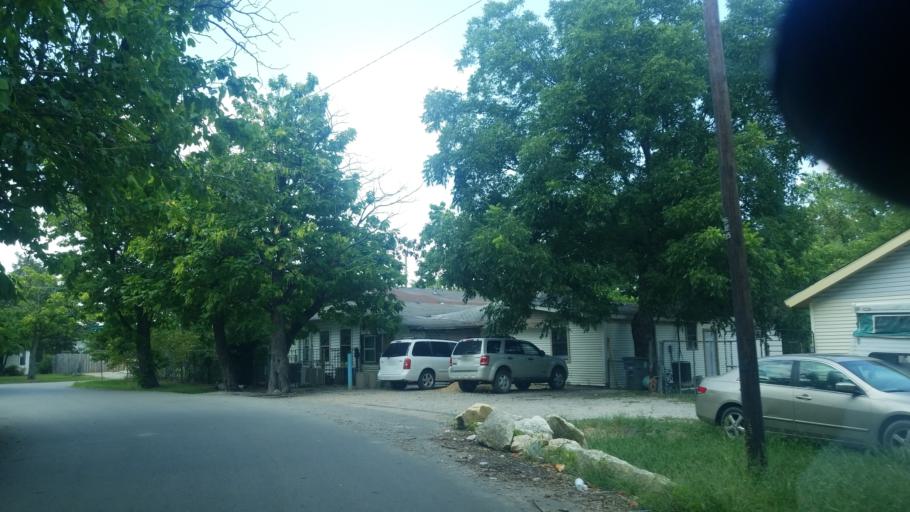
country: US
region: Texas
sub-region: Dallas County
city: Dallas
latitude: 32.7142
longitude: -96.7727
